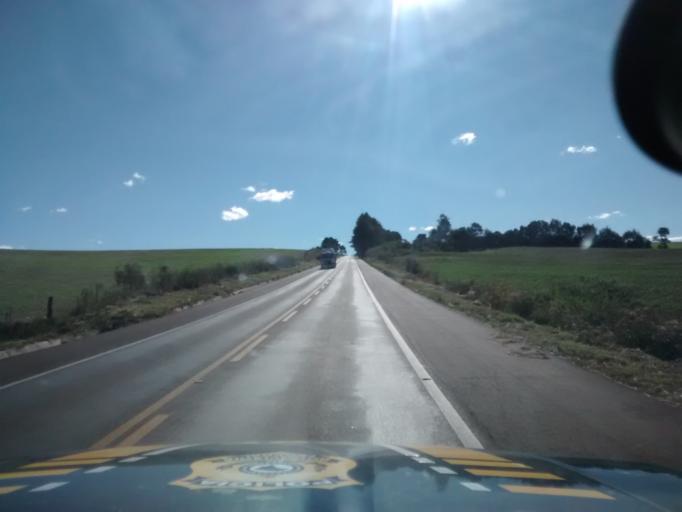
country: BR
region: Rio Grande do Sul
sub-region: Lagoa Vermelha
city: Lagoa Vermelha
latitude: -28.3108
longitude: -51.3625
